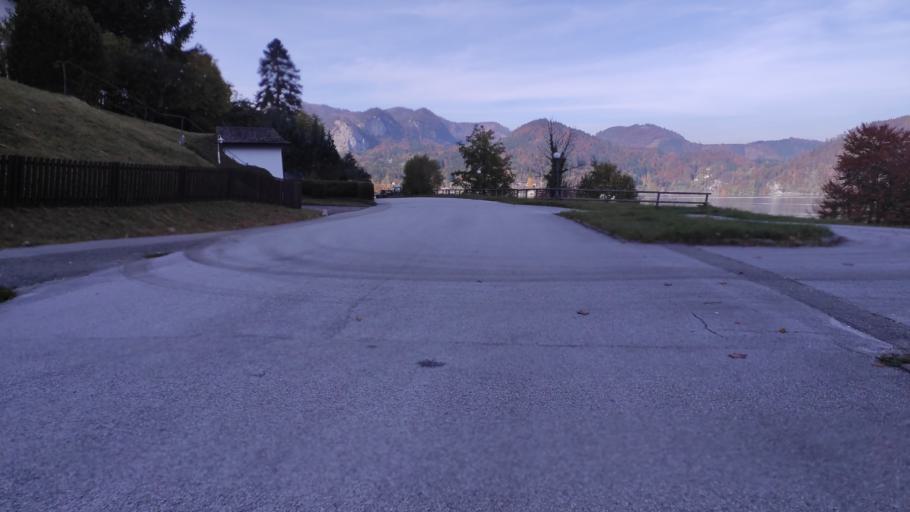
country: AT
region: Salzburg
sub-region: Politischer Bezirk Salzburg-Umgebung
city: Sankt Gilgen
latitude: 47.7545
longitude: 13.3720
